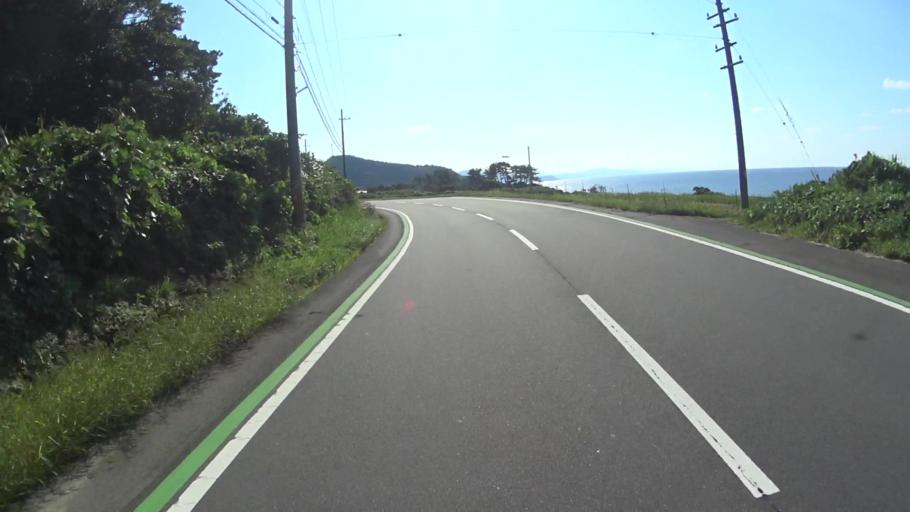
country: JP
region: Kyoto
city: Miyazu
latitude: 35.7242
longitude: 135.0855
